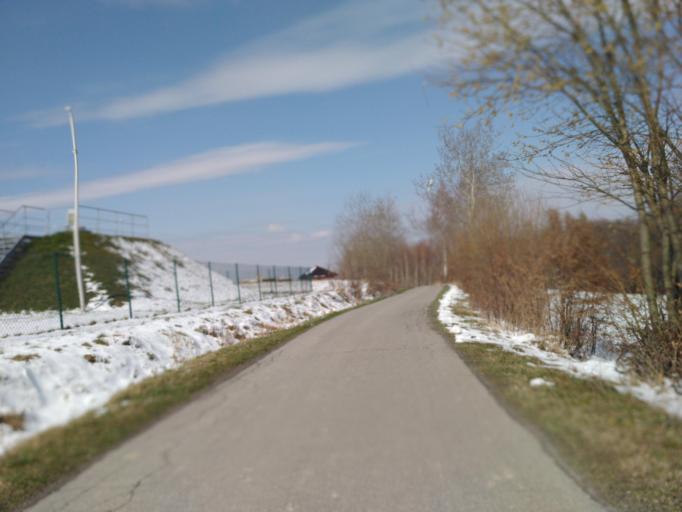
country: PL
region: Subcarpathian Voivodeship
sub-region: Powiat ropczycko-sedziszowski
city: Wielopole Skrzynskie
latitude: 49.9924
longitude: 21.5891
